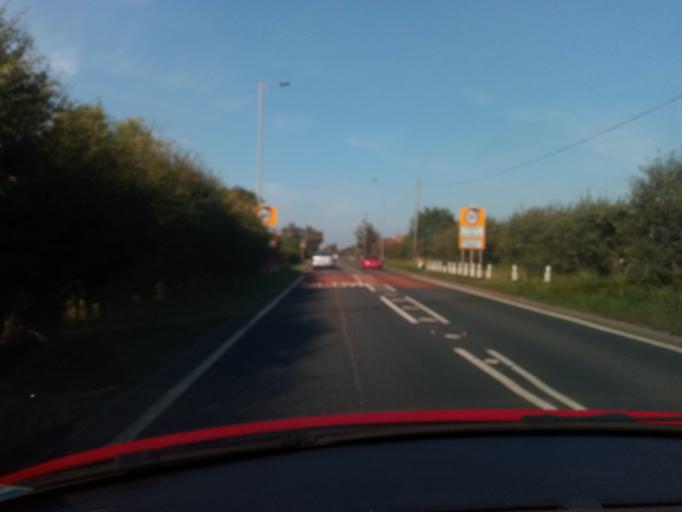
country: GB
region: England
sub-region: City of York
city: Skelton
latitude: 54.0272
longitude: -1.1595
